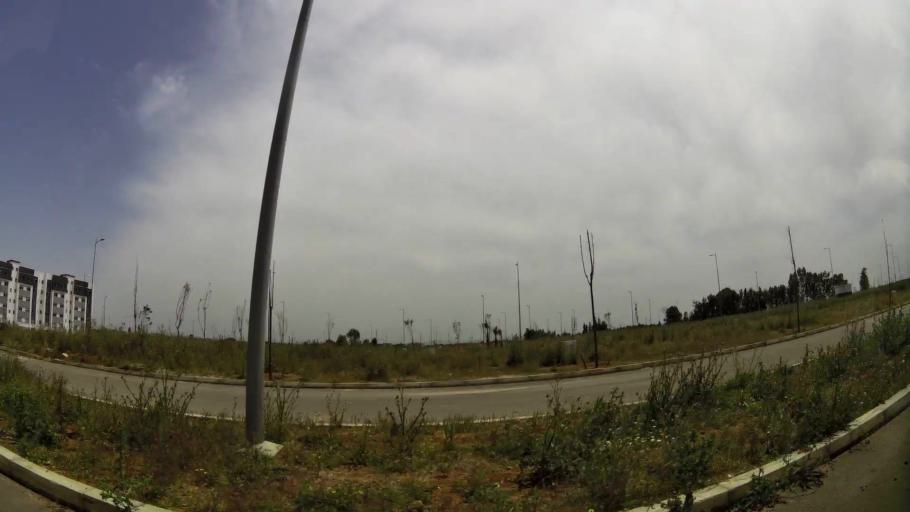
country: MA
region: Rabat-Sale-Zemmour-Zaer
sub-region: Khemisset
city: Khemisset
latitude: 33.8169
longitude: -6.0859
